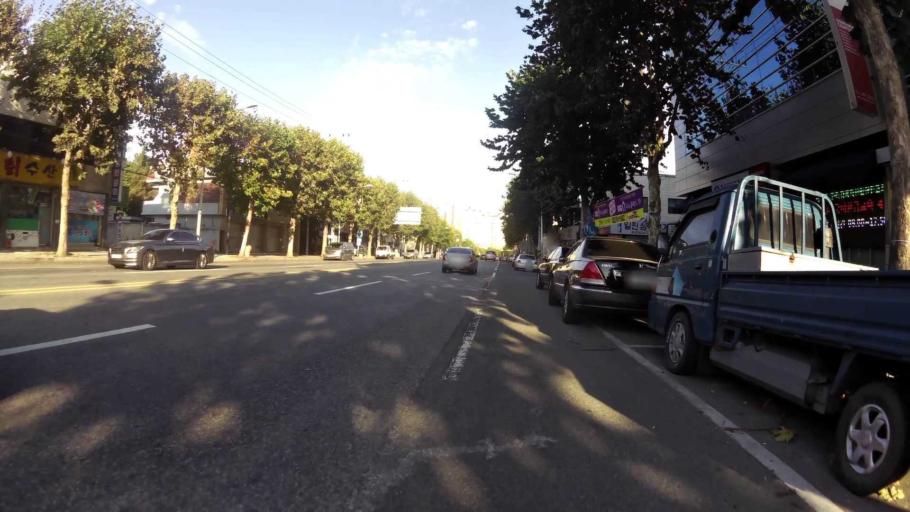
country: KR
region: Daegu
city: Daegu
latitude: 35.8669
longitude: 128.6316
